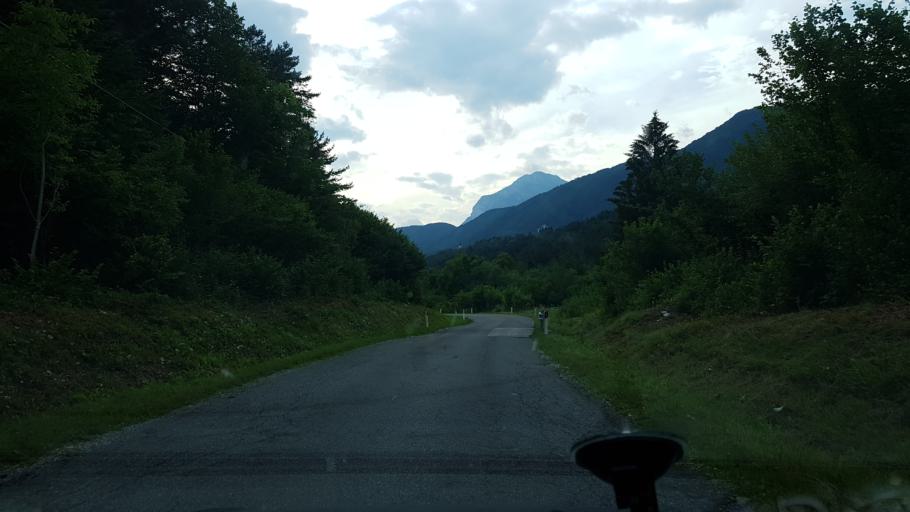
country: IT
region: Friuli Venezia Giulia
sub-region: Provincia di Udine
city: Prato
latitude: 46.3660
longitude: 13.3218
